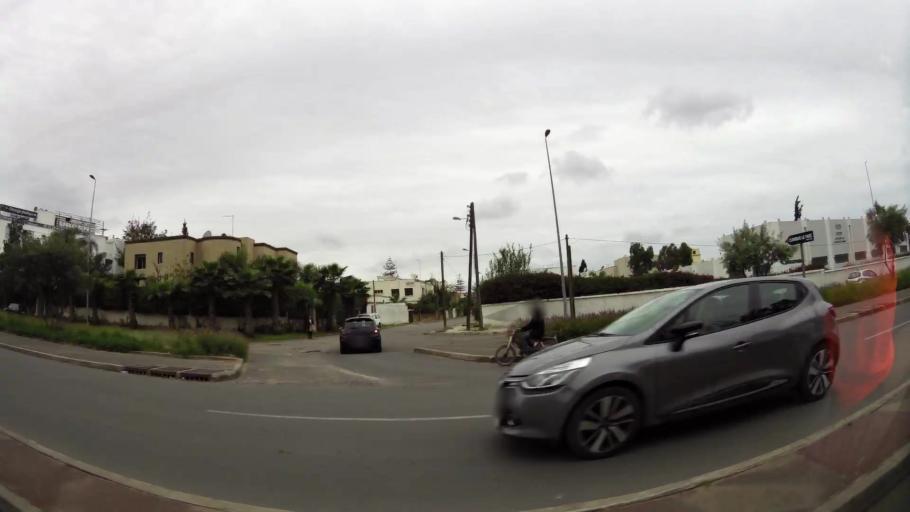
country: MA
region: Grand Casablanca
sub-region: Casablanca
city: Casablanca
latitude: 33.5644
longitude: -7.6146
